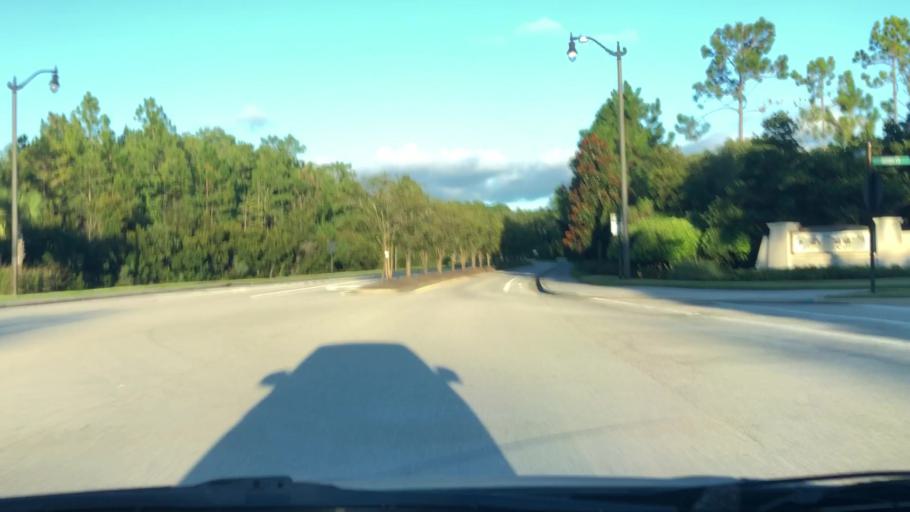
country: US
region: Florida
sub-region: Saint Johns County
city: Palm Valley
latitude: 30.1253
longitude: -81.4315
